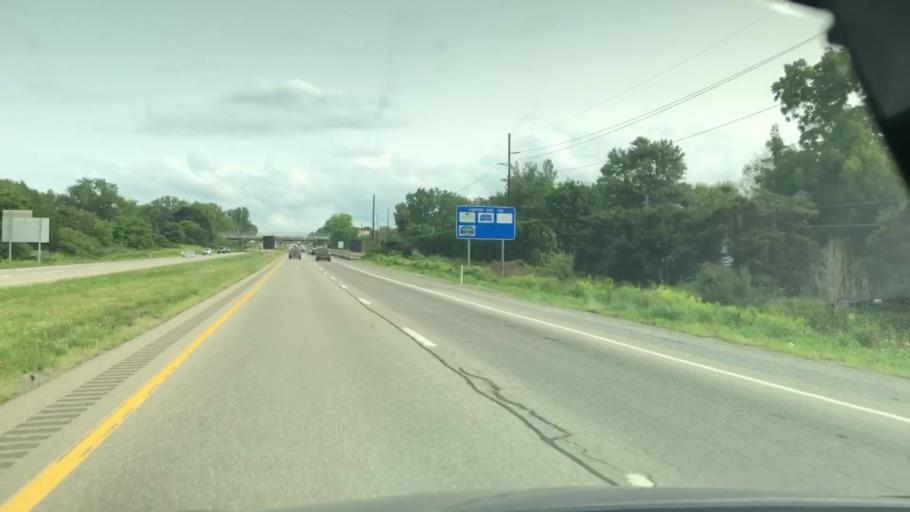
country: US
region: Pennsylvania
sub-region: Erie County
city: Erie
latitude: 42.0876
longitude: -80.1176
